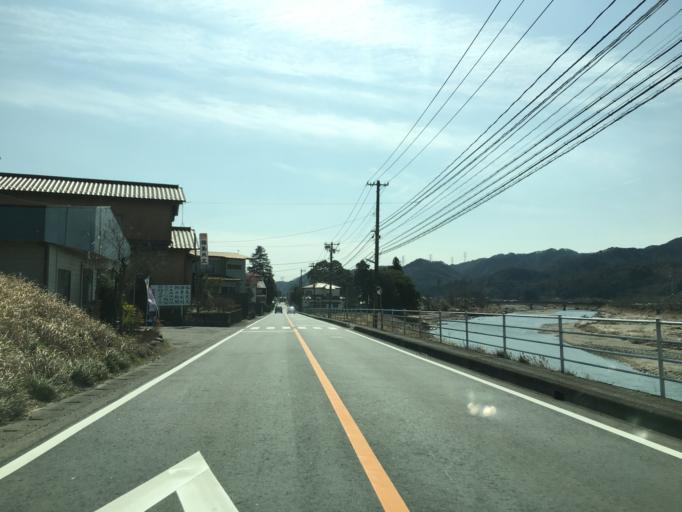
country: JP
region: Ibaraki
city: Daigo
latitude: 36.9482
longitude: 140.4143
